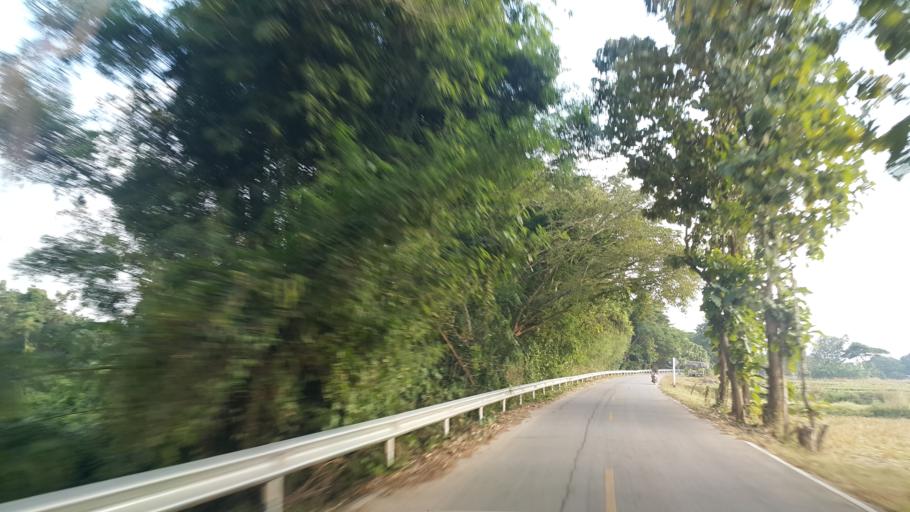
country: TH
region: Lampang
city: Sop Prap
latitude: 17.9147
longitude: 99.3301
